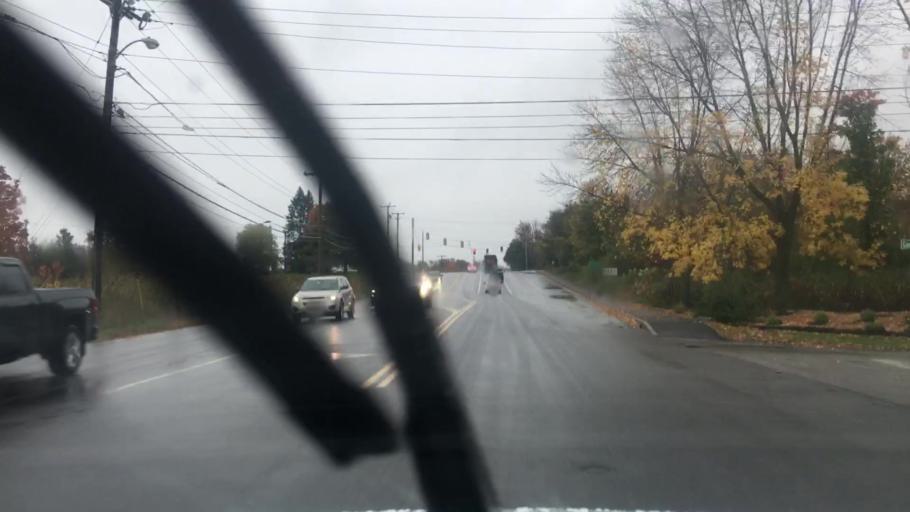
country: US
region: Maine
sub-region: Cumberland County
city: South Portland Gardens
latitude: 43.6356
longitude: -70.3505
